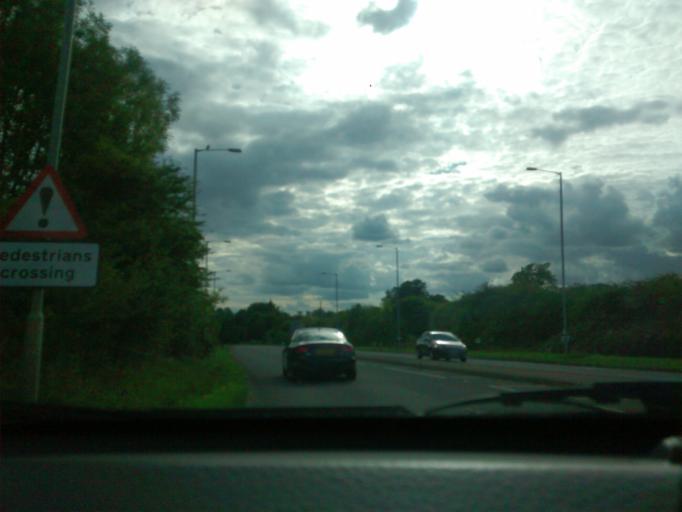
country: GB
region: England
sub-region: Norfolk
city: Downham Market
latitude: 52.5924
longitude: 0.3915
